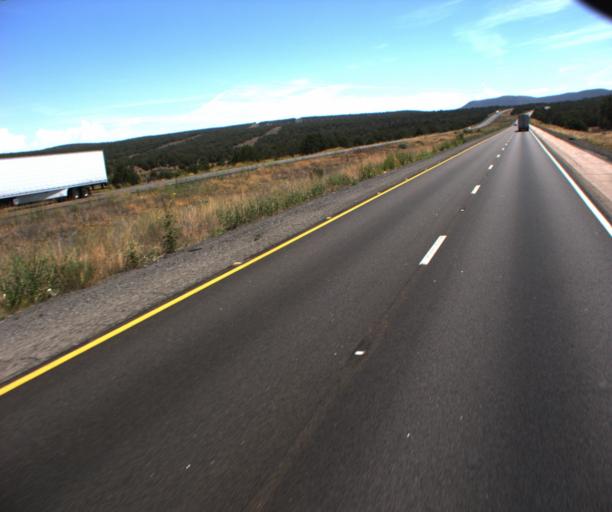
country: US
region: Arizona
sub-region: Mohave County
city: Peach Springs
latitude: 35.1909
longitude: -113.3445
